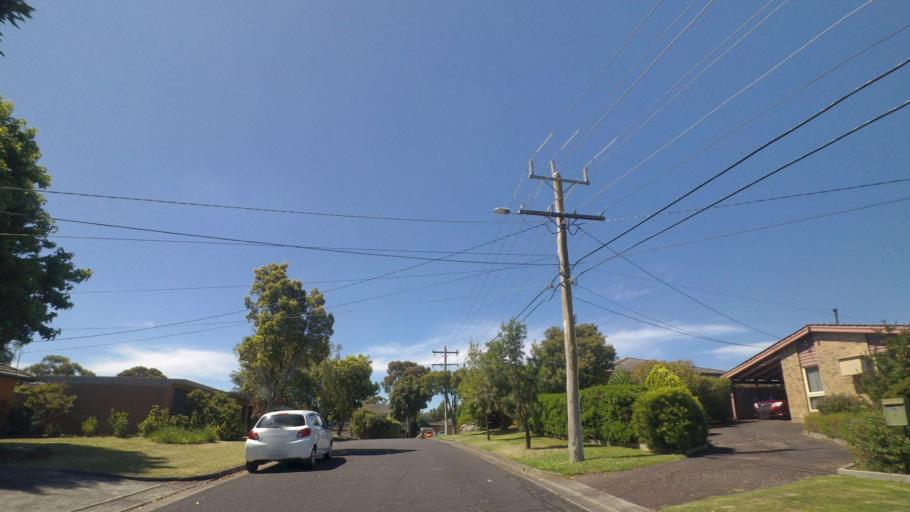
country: AU
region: Victoria
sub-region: Manningham
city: Park Orchards
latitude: -37.7976
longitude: 145.2292
